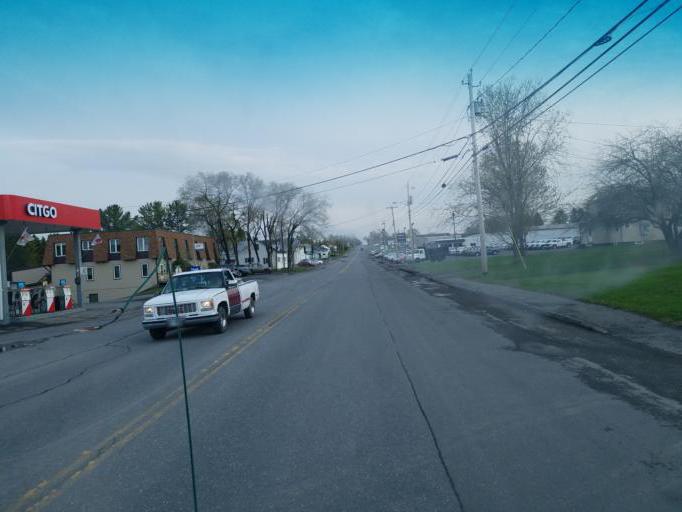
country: US
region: Maine
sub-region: Aroostook County
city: Caribou
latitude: 46.8480
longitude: -68.0108
